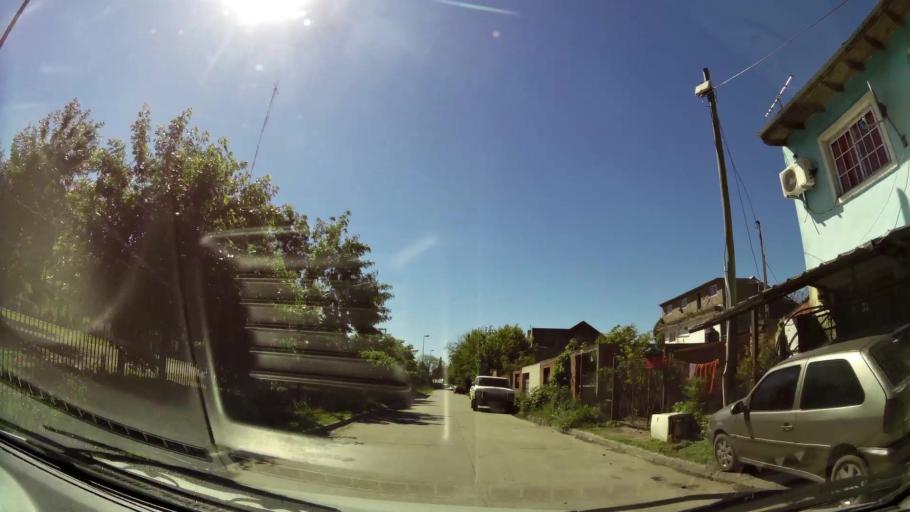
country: AR
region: Buenos Aires
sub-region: Partido de Almirante Brown
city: Adrogue
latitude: -34.7850
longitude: -58.3511
